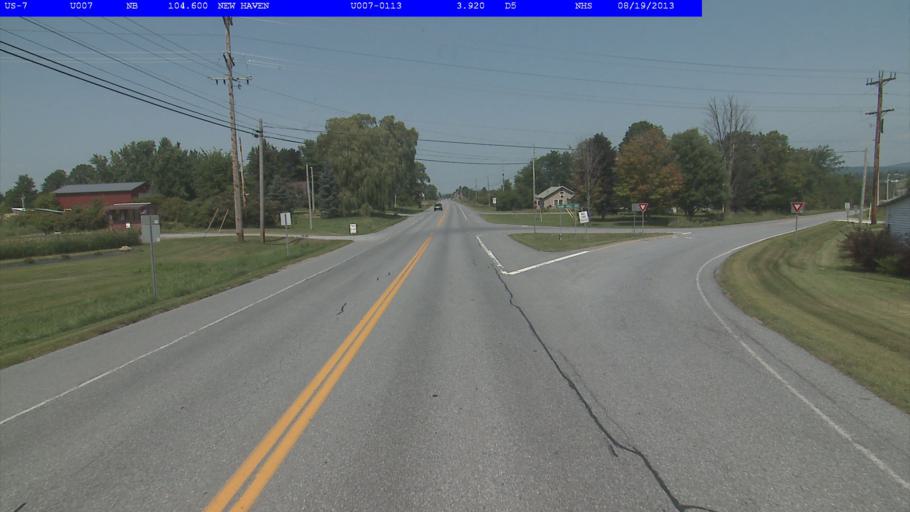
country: US
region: Vermont
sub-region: Addison County
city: Middlebury (village)
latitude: 44.1018
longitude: -73.1734
